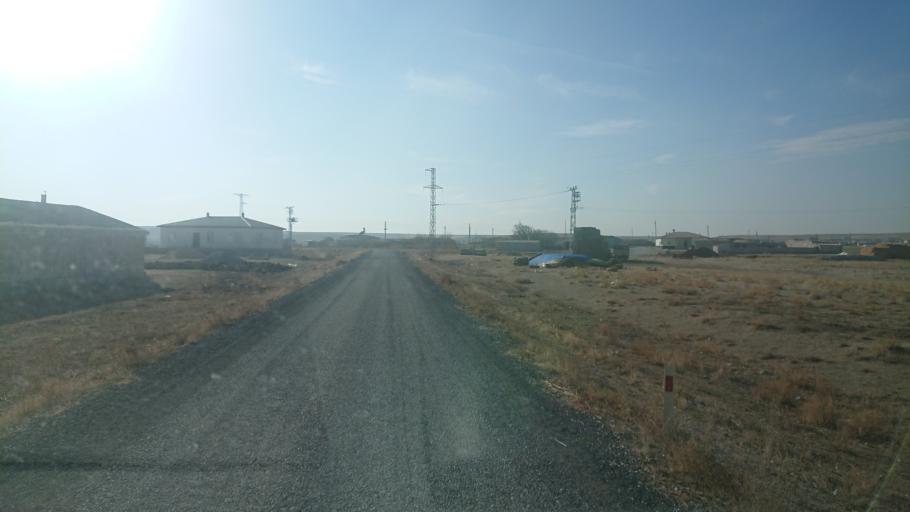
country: TR
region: Aksaray
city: Sultanhani
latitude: 38.0391
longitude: 33.6081
